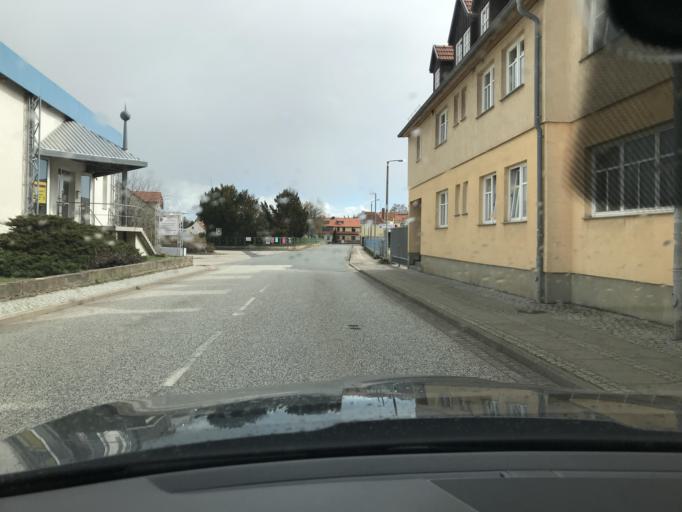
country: DE
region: Saxony-Anhalt
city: Ballenstedt
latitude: 51.7231
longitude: 11.2450
